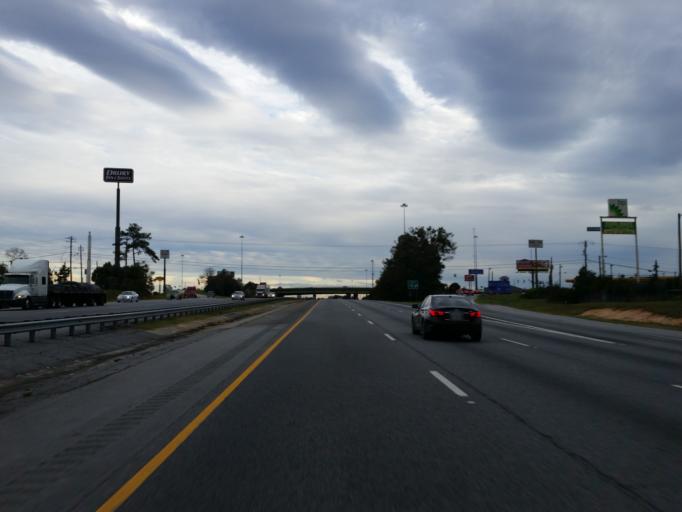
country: US
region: Georgia
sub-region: Lowndes County
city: Remerton
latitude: 30.8484
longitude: -83.3321
